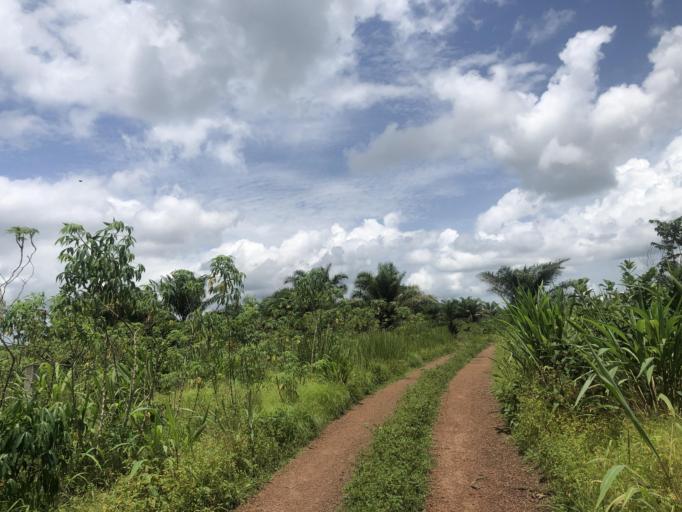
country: SL
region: Northern Province
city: Magburaka
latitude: 8.7102
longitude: -11.9407
